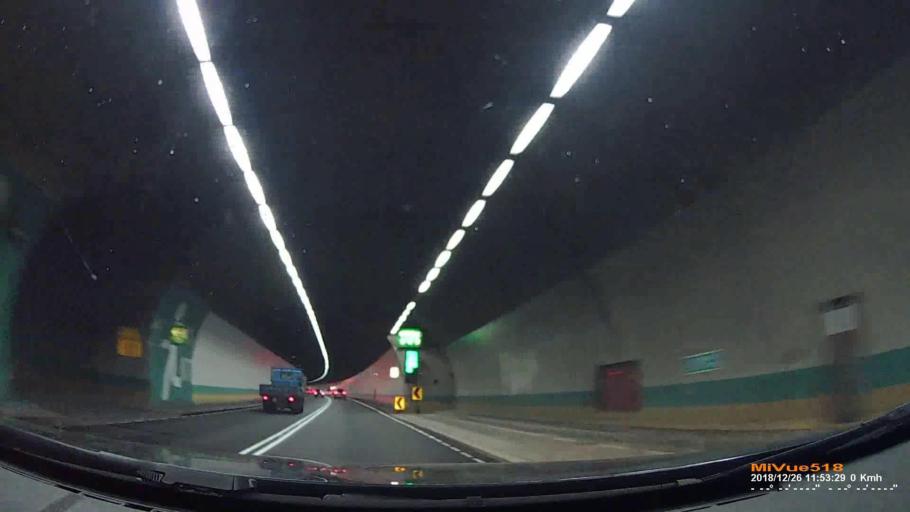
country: TW
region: Taiwan
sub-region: Keelung
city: Keelung
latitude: 24.9581
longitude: 121.6929
